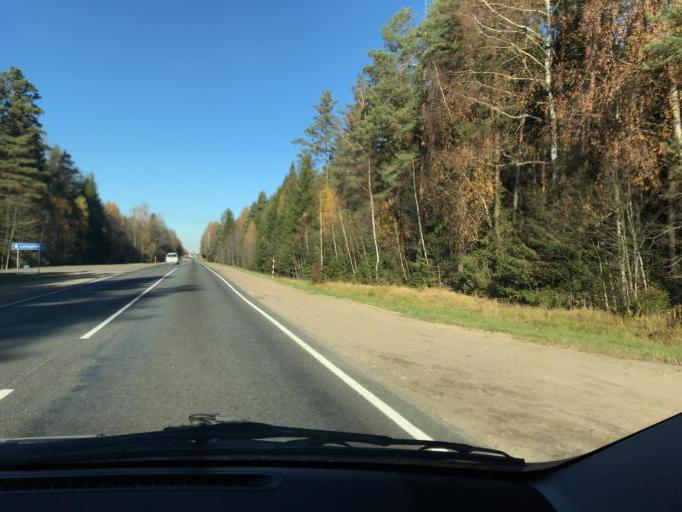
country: BY
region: Vitebsk
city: Polatsk
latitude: 55.4387
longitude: 28.7777
